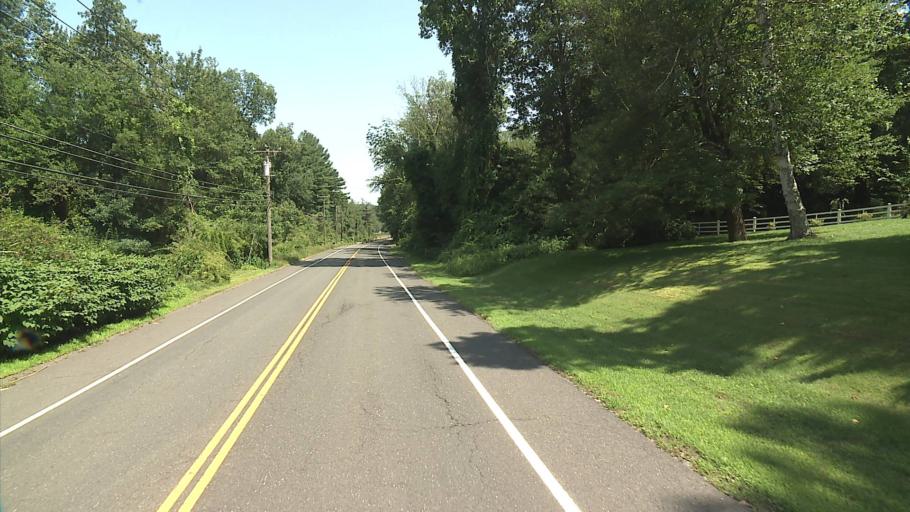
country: US
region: Connecticut
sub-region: Hartford County
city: Salmon Brook
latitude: 41.9549
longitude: -72.8221
